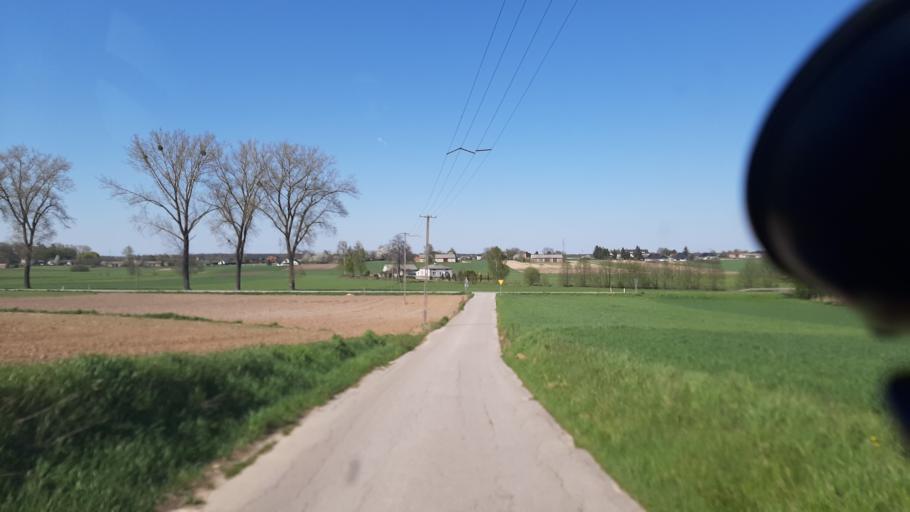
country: PL
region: Lublin Voivodeship
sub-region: Powiat lubelski
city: Jastkow
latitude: 51.3436
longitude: 22.3935
